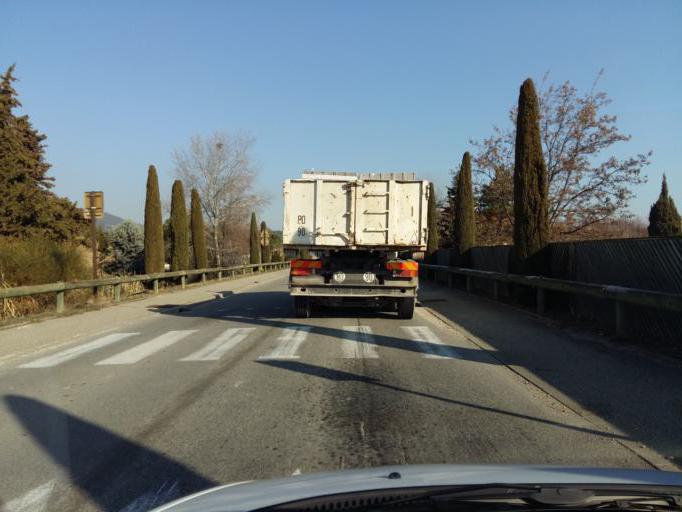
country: FR
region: Provence-Alpes-Cote d'Azur
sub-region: Departement du Vaucluse
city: Sablet
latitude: 44.2438
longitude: 5.0174
